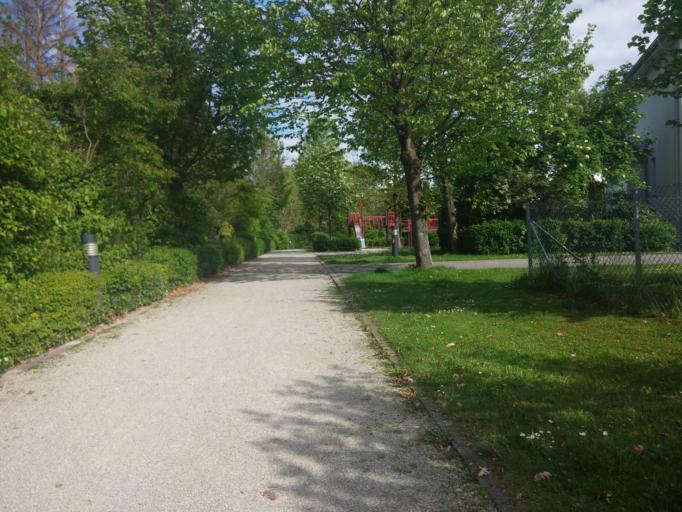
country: DE
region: Bavaria
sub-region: Upper Bavaria
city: Bogenhausen
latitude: 48.1487
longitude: 11.6460
